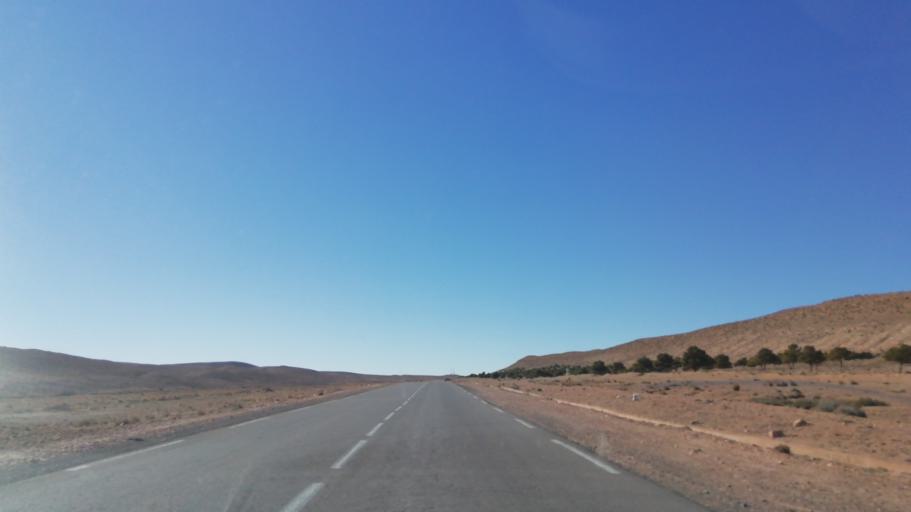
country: DZ
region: El Bayadh
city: El Bayadh
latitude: 33.6856
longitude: 1.4590
